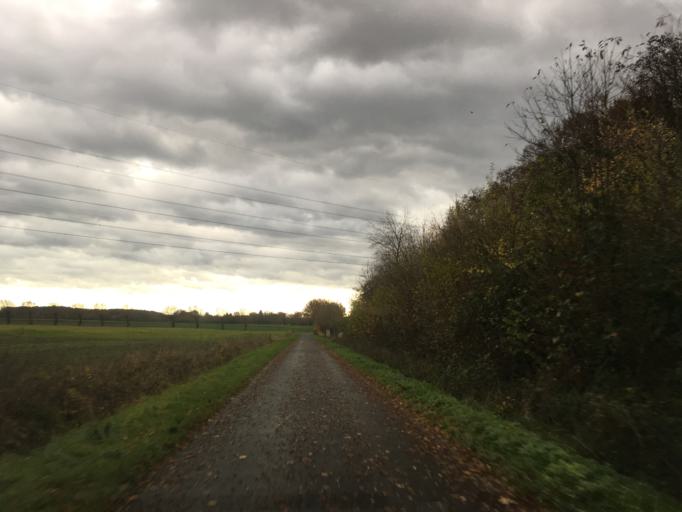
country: DE
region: North Rhine-Westphalia
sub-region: Regierungsbezirk Munster
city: Greven
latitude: 52.0340
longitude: 7.5481
